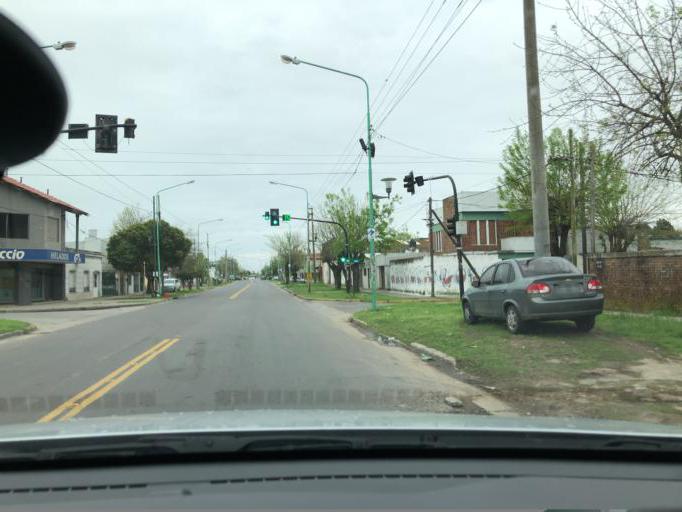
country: AR
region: Buenos Aires
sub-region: Partido de Ensenada
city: Ensenada
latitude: -34.8585
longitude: -57.9151
